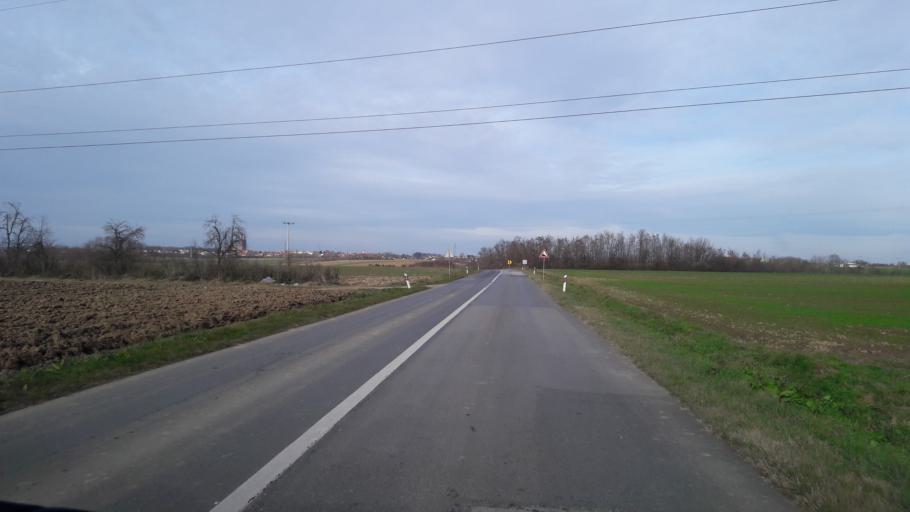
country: HR
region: Osjecko-Baranjska
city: Piskorevci
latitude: 45.2885
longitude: 18.4329
